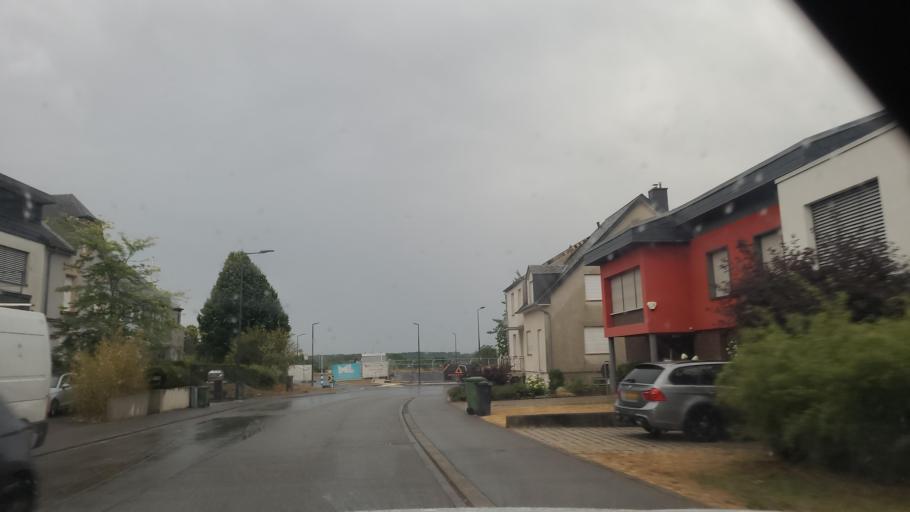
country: LU
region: Luxembourg
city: Hautcharage
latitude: 49.5792
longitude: 5.9113
